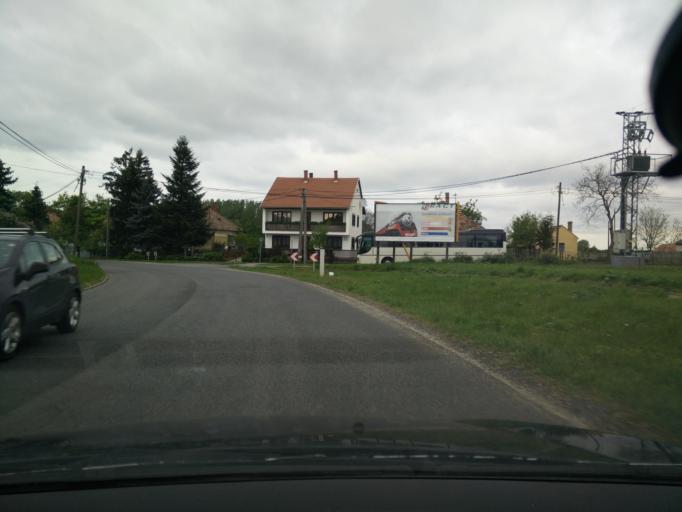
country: HU
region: Veszprem
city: Papa
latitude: 47.3923
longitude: 17.4765
